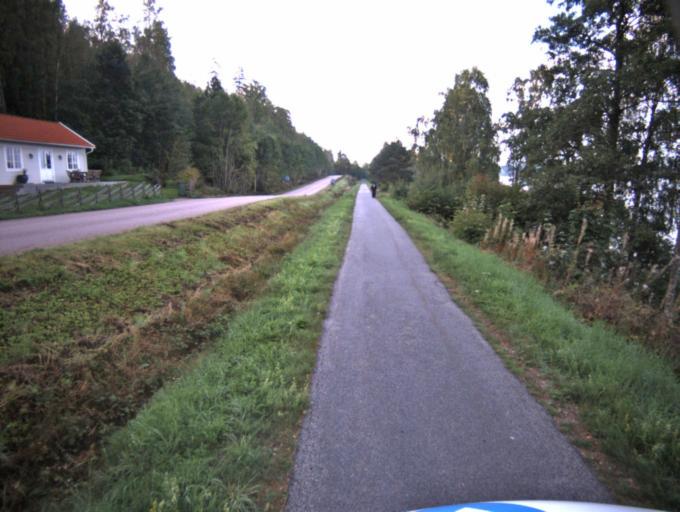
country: SE
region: Vaestra Goetaland
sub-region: Ulricehamns Kommun
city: Ulricehamn
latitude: 57.7512
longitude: 13.3944
